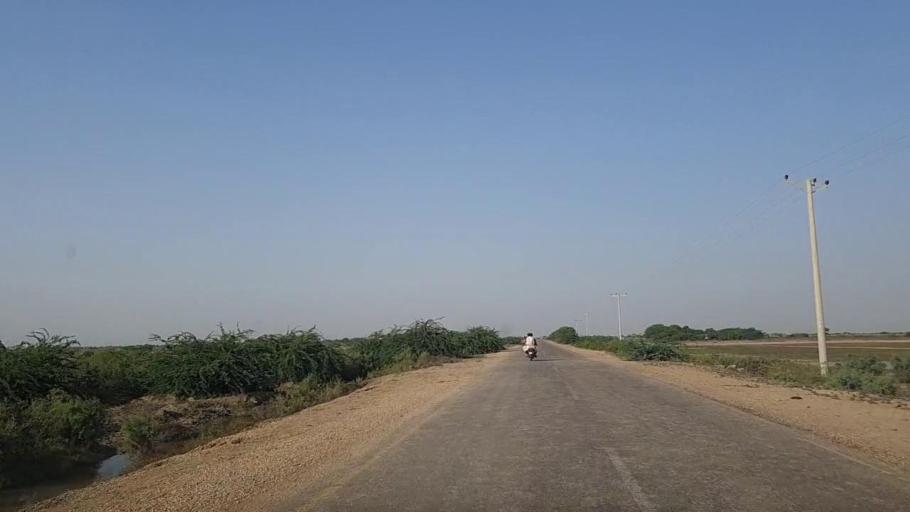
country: PK
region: Sindh
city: Mirpur Batoro
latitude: 24.6076
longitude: 68.4025
